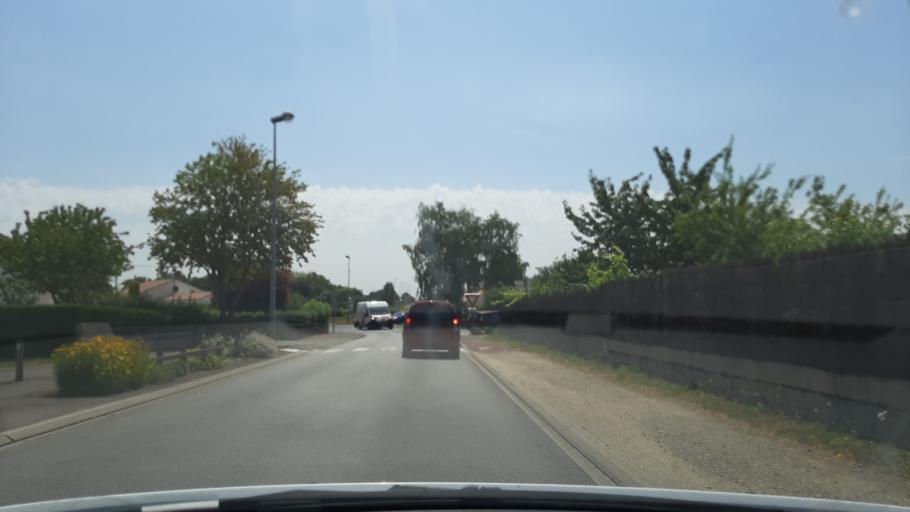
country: FR
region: Pays de la Loire
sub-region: Departement de la Vendee
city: Le Poire-sur-Vie
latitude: 46.7663
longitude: -1.4989
